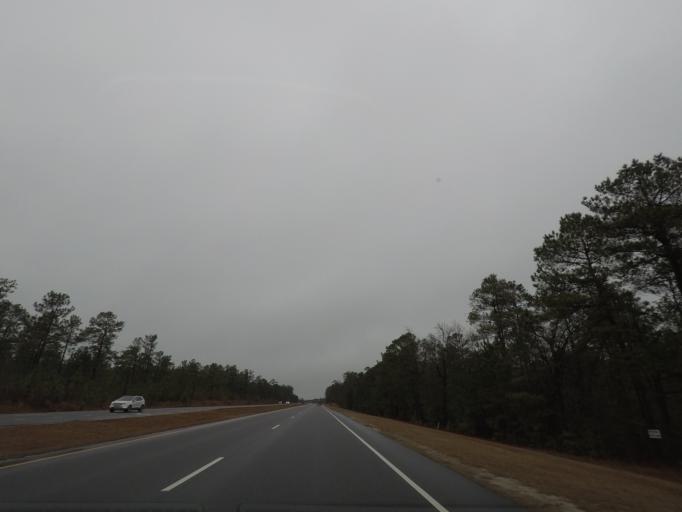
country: US
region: North Carolina
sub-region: Cumberland County
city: Spring Lake
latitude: 35.2368
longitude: -79.0202
